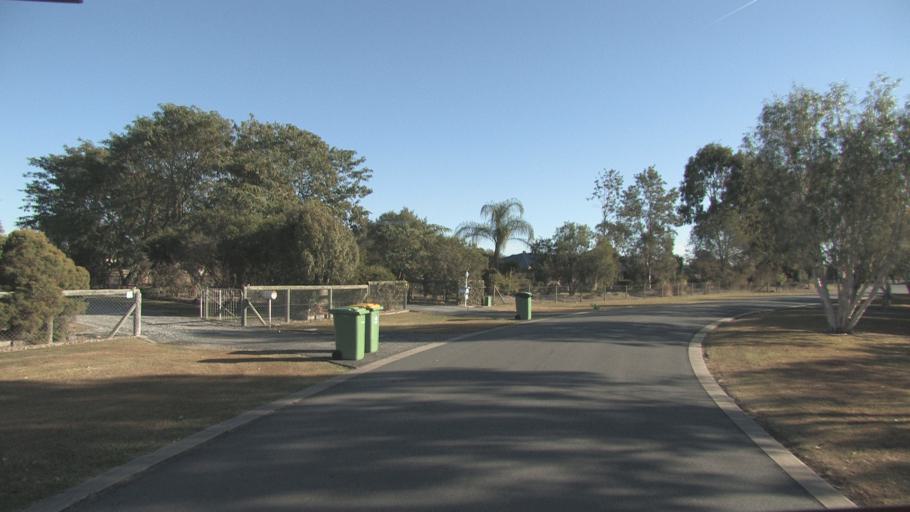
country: AU
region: Queensland
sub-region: Logan
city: North Maclean
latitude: -27.8263
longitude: 153.0077
